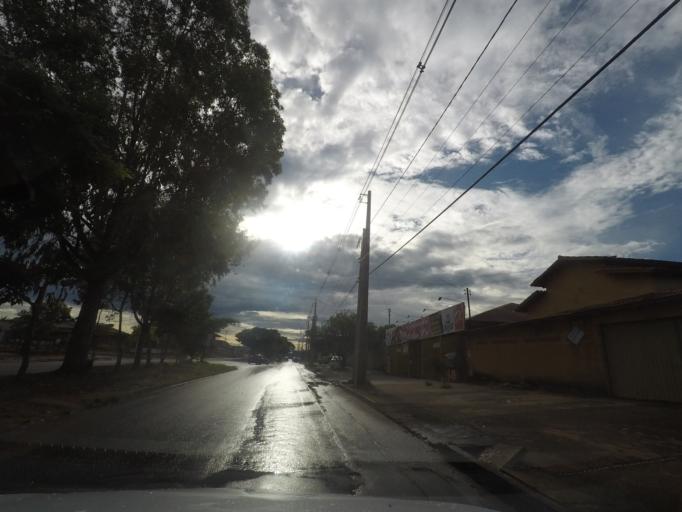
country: BR
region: Goias
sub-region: Aparecida De Goiania
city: Aparecida de Goiania
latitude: -16.7611
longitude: -49.3533
